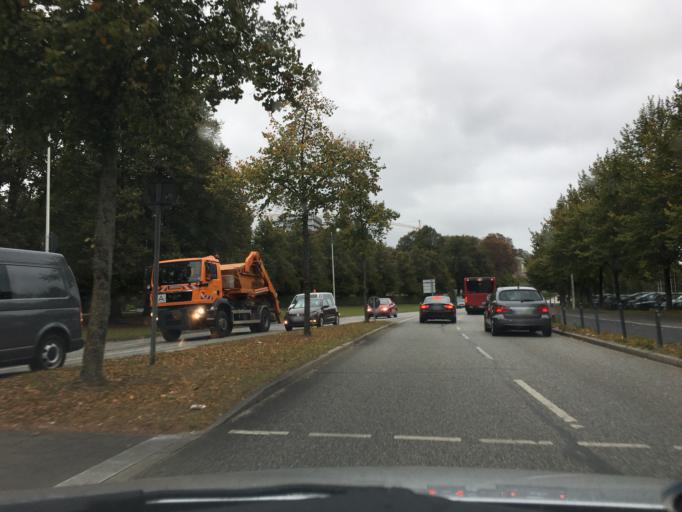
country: DE
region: Schleswig-Holstein
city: Kiel
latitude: 54.3253
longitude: 10.1448
